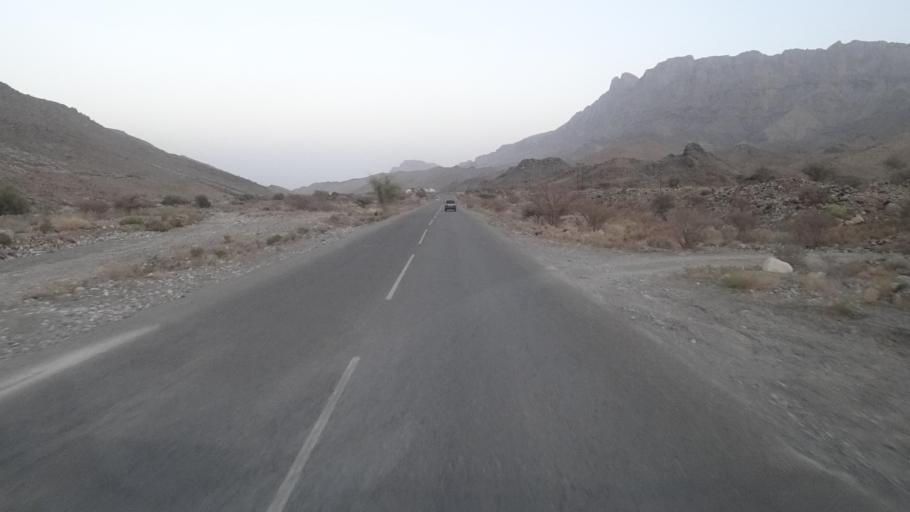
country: OM
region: Muhafazat ad Dakhiliyah
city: Bahla'
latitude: 23.1650
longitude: 57.1612
